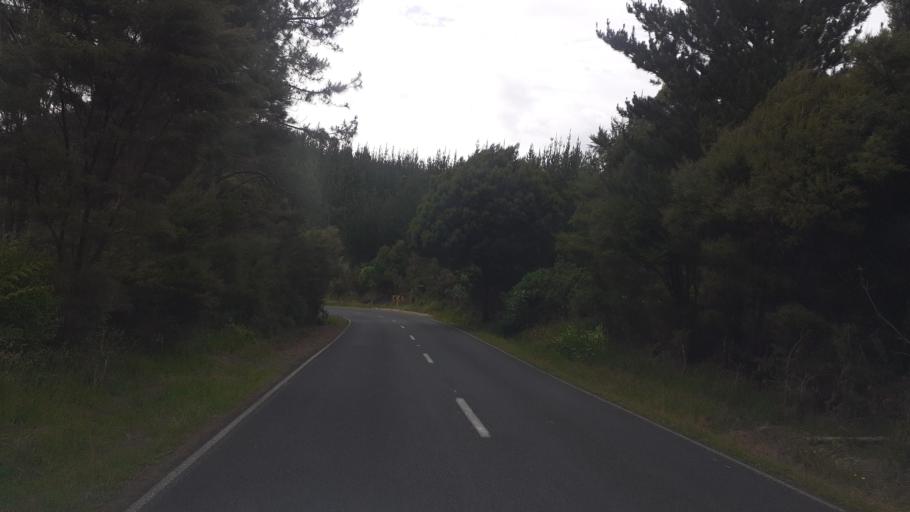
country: NZ
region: Northland
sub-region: Far North District
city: Kerikeri
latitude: -35.2252
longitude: 174.0052
